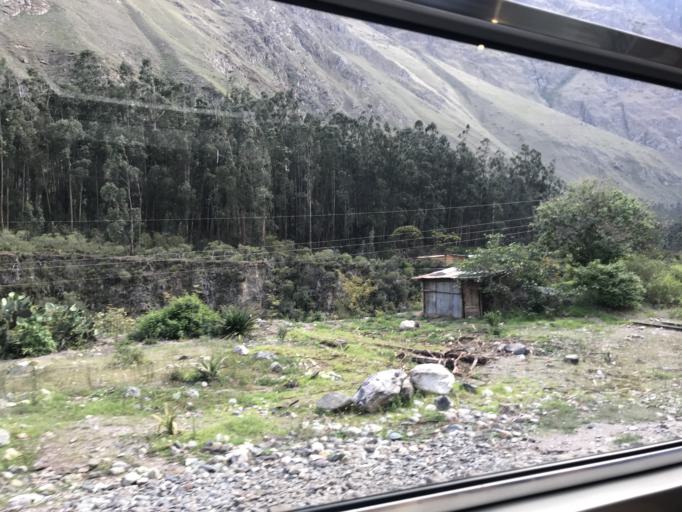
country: PE
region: Cusco
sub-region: Provincia de Urubamba
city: Ollantaytambo
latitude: -13.2253
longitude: -72.4334
